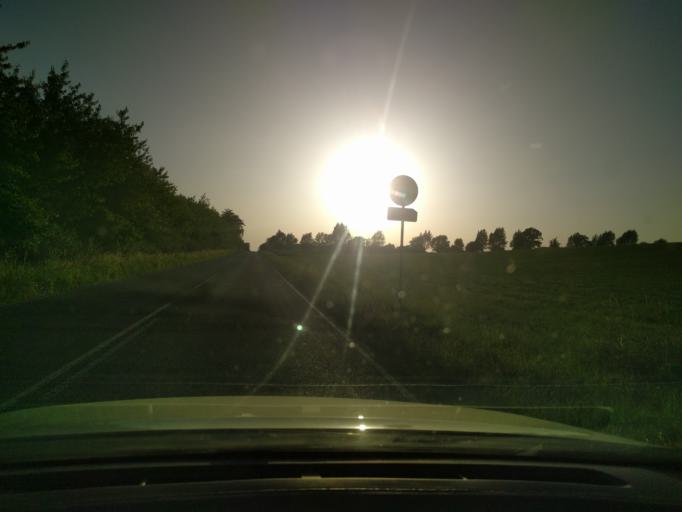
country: DK
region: Zealand
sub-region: Vordingborg Kommune
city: Praesto
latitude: 55.1176
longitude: 11.9889
